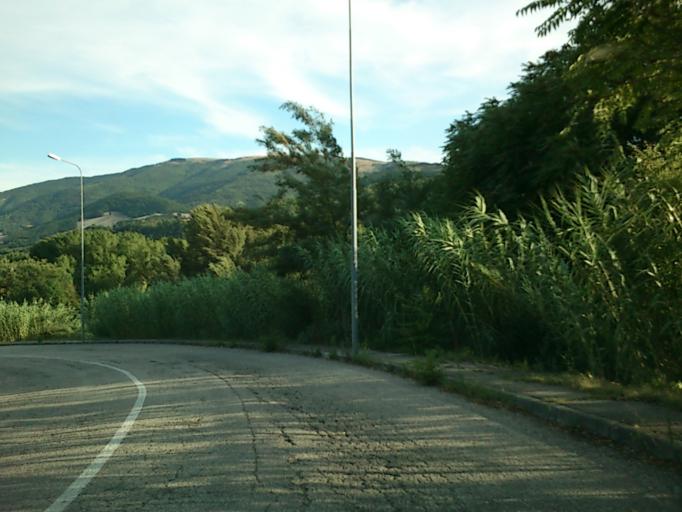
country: IT
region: The Marches
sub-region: Provincia di Pesaro e Urbino
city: Canavaccio
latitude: 43.6977
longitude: 12.6882
